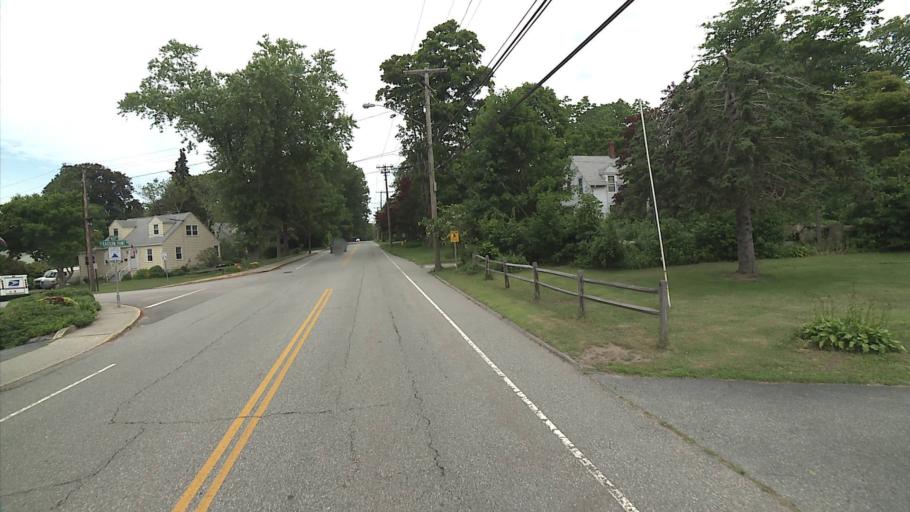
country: US
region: Connecticut
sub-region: New London County
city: Groton
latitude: 41.3272
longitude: -72.0732
